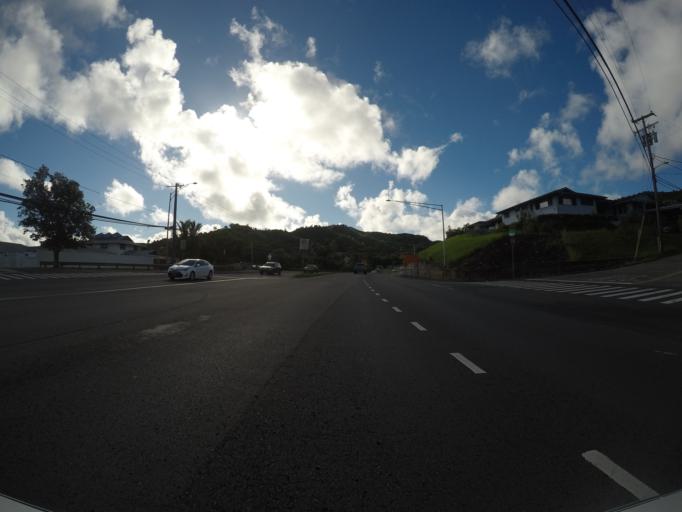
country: US
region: Hawaii
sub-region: Honolulu County
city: Kane'ohe
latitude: 21.4110
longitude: -157.7741
